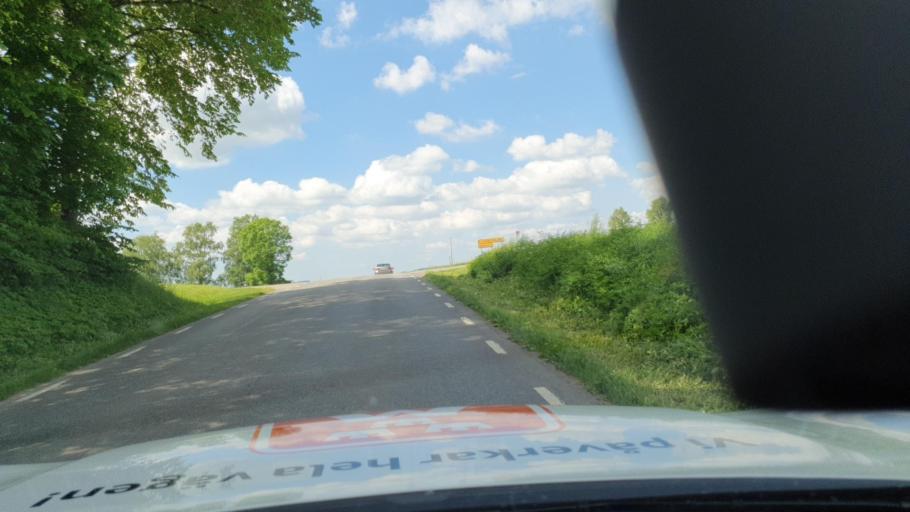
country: SE
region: Vaestra Goetaland
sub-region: Falkopings Kommun
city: Falkoeping
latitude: 58.1103
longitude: 13.5898
